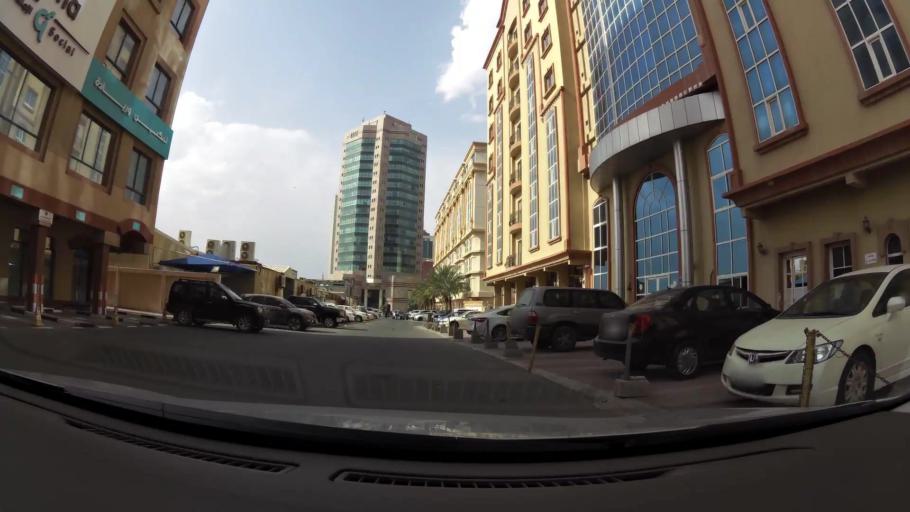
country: QA
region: Baladiyat ad Dawhah
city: Doha
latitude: 25.2755
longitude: 51.5094
